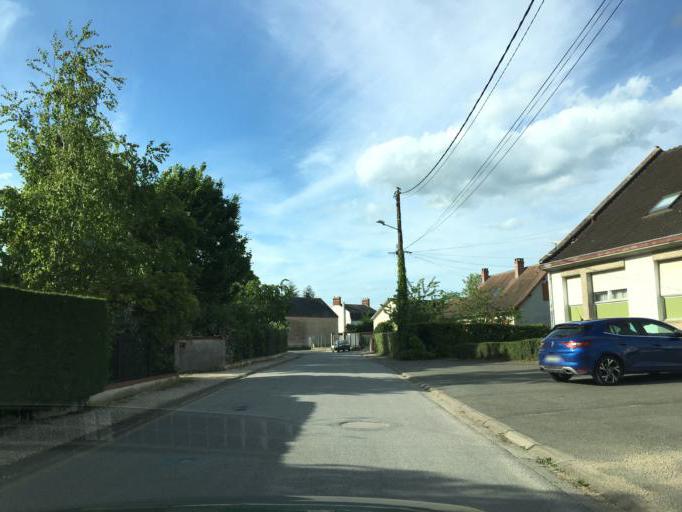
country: FR
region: Centre
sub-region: Departement du Loiret
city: Clery-Saint-Andre
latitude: 47.8215
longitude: 1.7589
